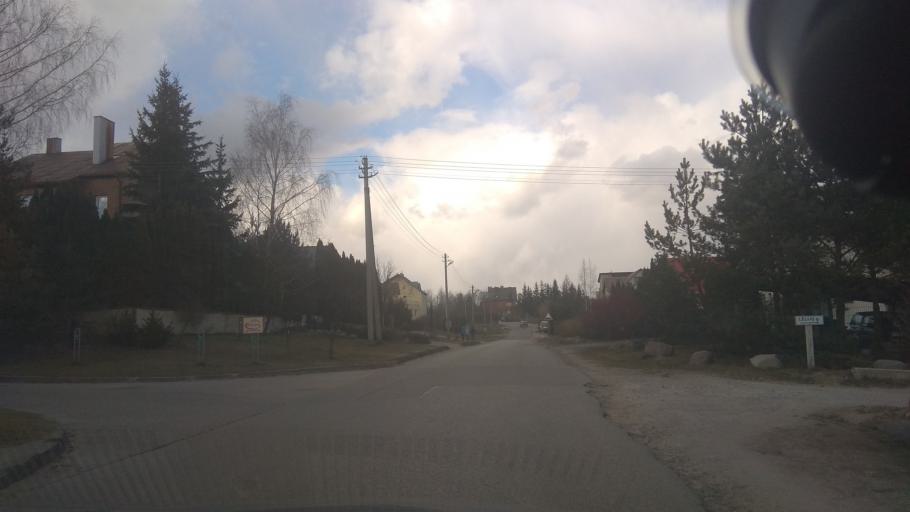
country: LT
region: Vilnius County
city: Pasilaiciai
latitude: 54.7382
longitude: 25.2022
